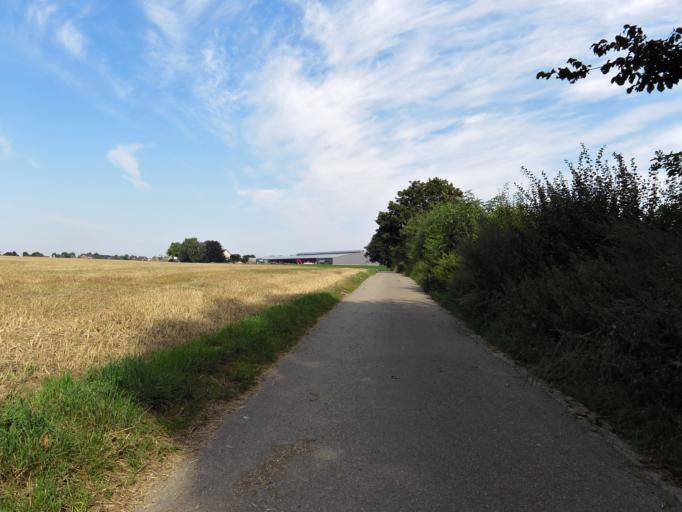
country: DE
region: North Rhine-Westphalia
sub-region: Regierungsbezirk Koln
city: Alsdorf
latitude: 50.8980
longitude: 6.1455
